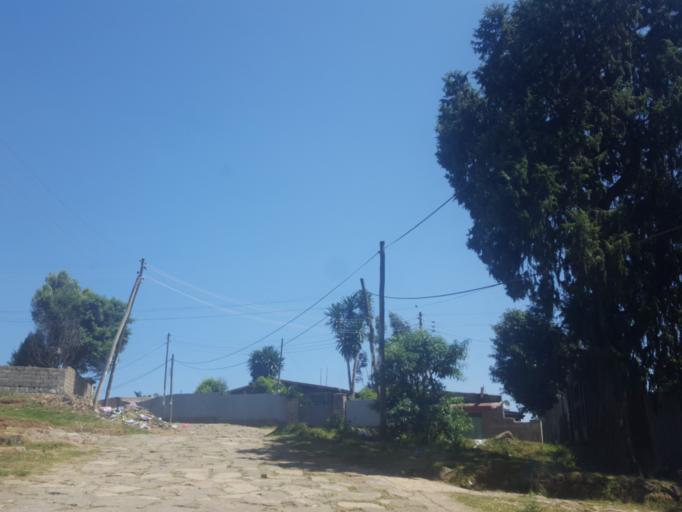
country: ET
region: Adis Abeba
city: Addis Ababa
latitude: 9.0631
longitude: 38.7412
